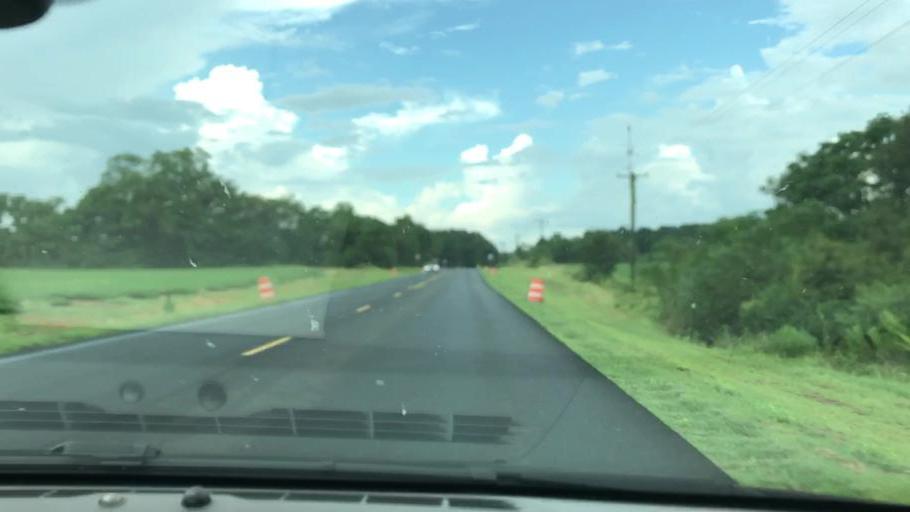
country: US
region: Georgia
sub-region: Early County
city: Blakely
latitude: 31.3982
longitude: -84.9550
